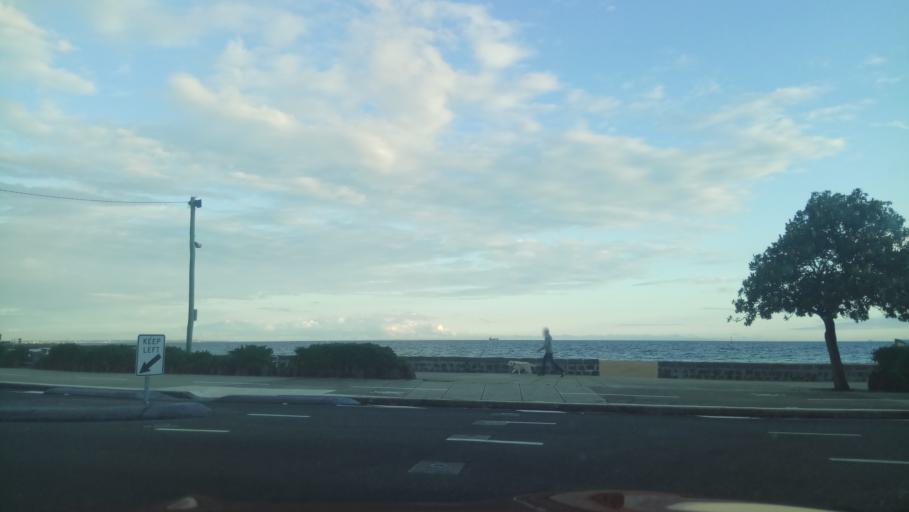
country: AU
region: Victoria
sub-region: Hobsons Bay
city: Williamstown
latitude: -37.8665
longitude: 144.8899
